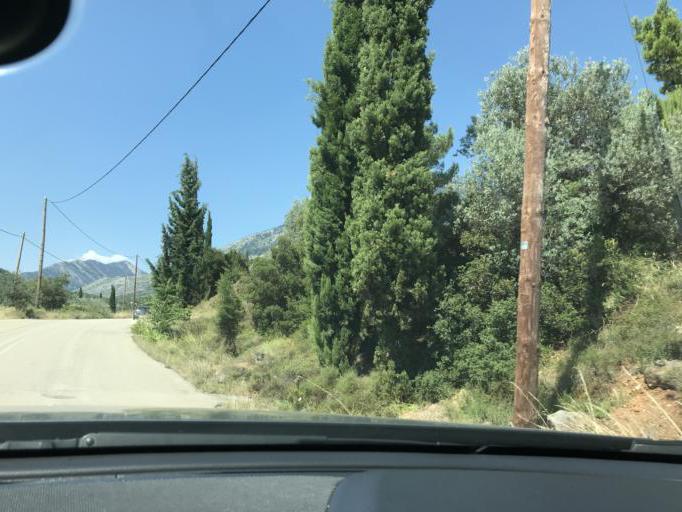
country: GR
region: Central Greece
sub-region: Nomos Voiotias
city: Distomo
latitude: 38.5109
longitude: 22.7195
